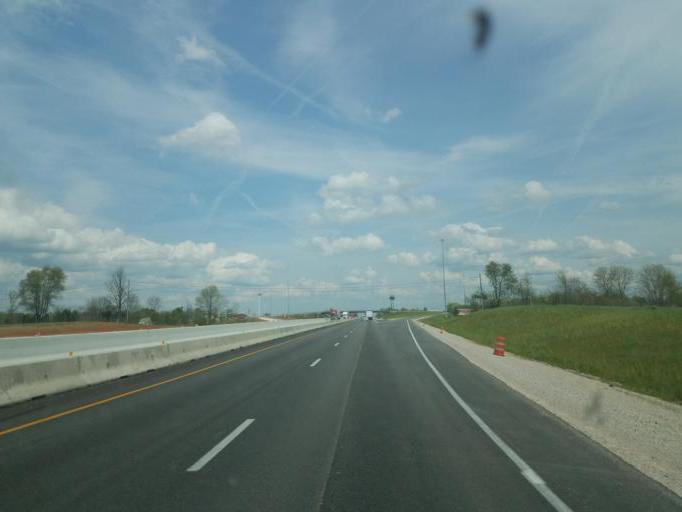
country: US
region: Kentucky
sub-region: Larue County
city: Hodgenville
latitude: 37.5165
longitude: -85.8858
